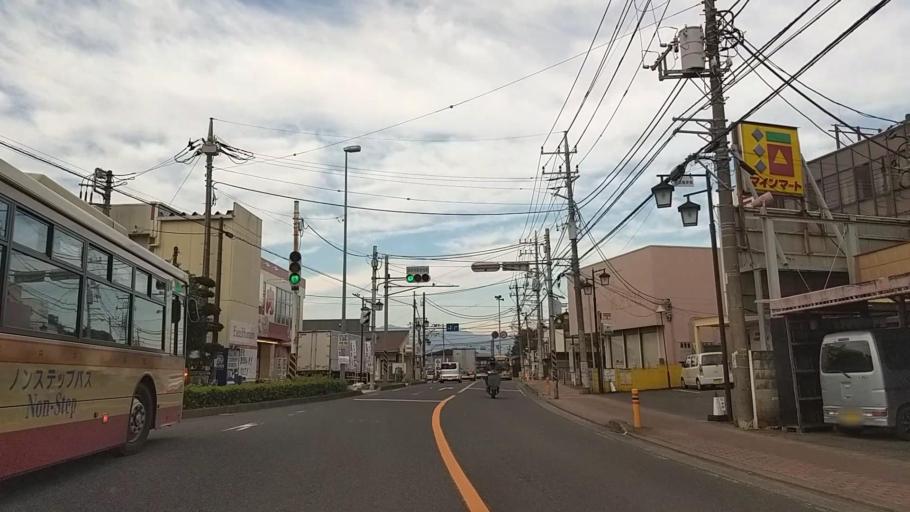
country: JP
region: Kanagawa
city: Atsugi
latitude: 35.4038
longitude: 139.4148
